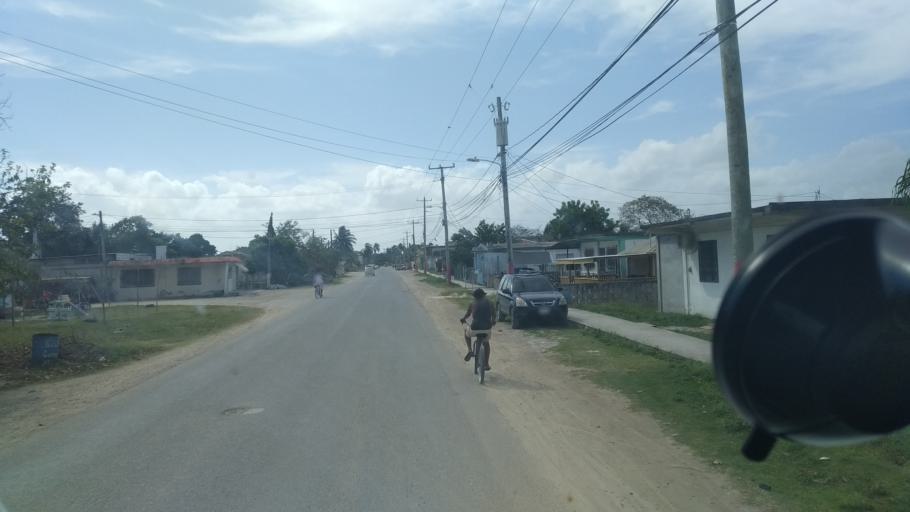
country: BZ
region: Corozal
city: Corozal
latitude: 18.4014
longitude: -88.3828
